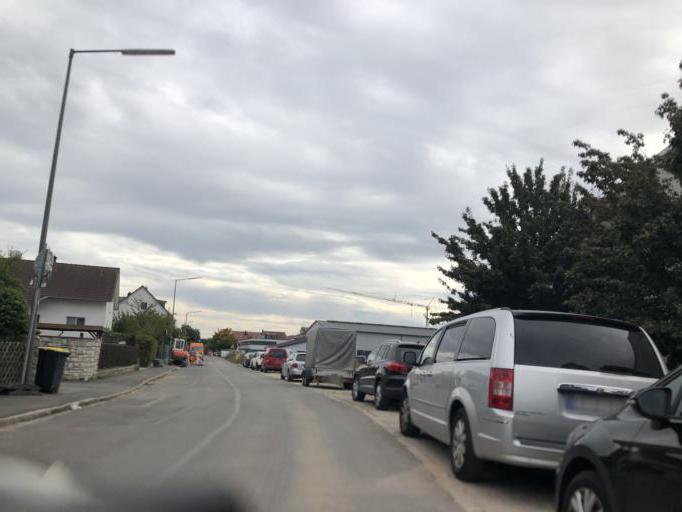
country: DE
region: Bavaria
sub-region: Regierungsbezirk Mittelfranken
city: Erlangen
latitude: 49.5550
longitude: 10.9949
